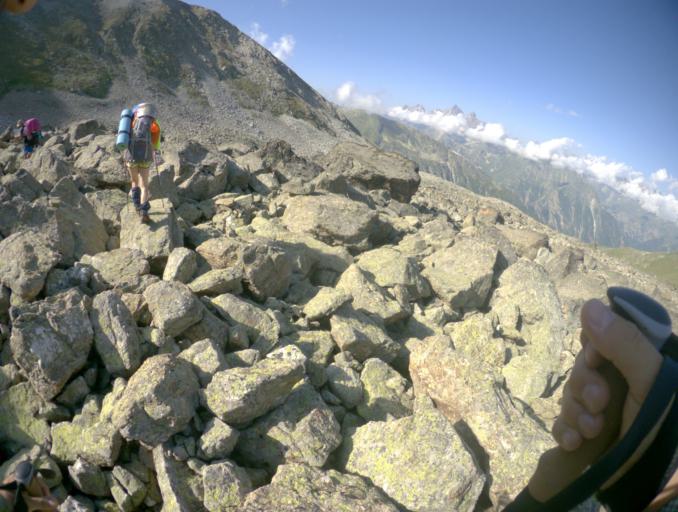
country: RU
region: Karachayevo-Cherkesiya
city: Uchkulan
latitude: 43.3091
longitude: 42.0660
